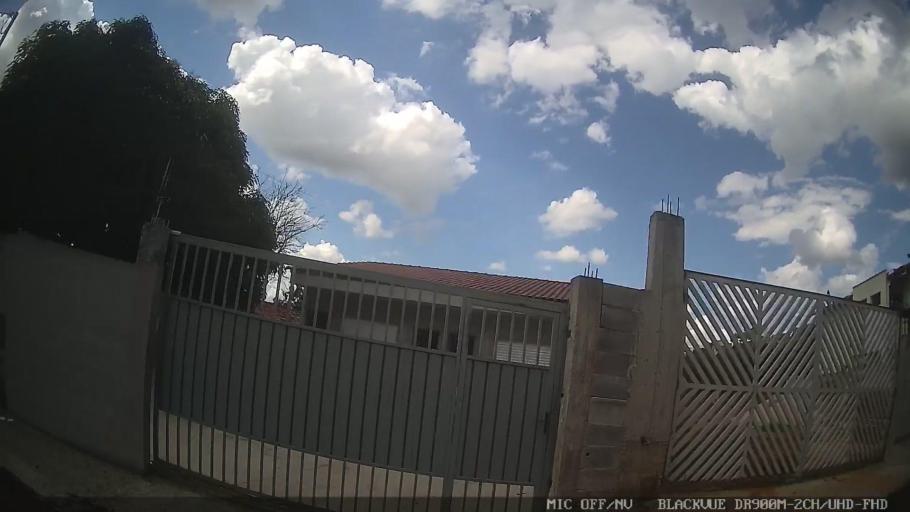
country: BR
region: Minas Gerais
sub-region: Extrema
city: Extrema
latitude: -22.8595
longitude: -46.3125
